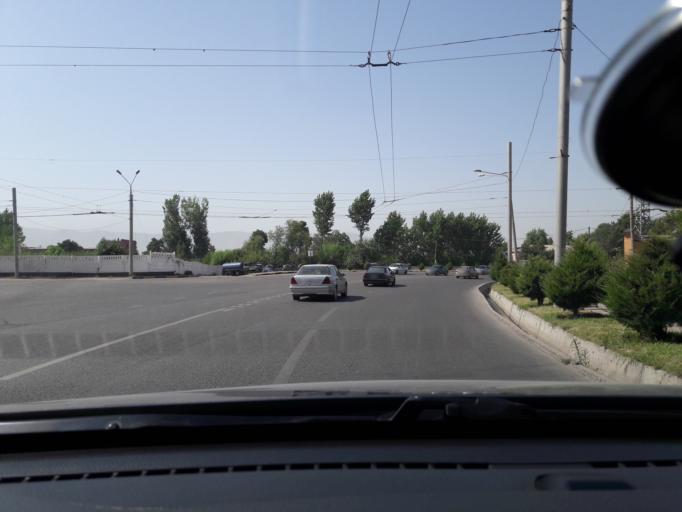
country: TJ
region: Dushanbe
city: Dushanbe
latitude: 38.5041
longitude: 68.7617
